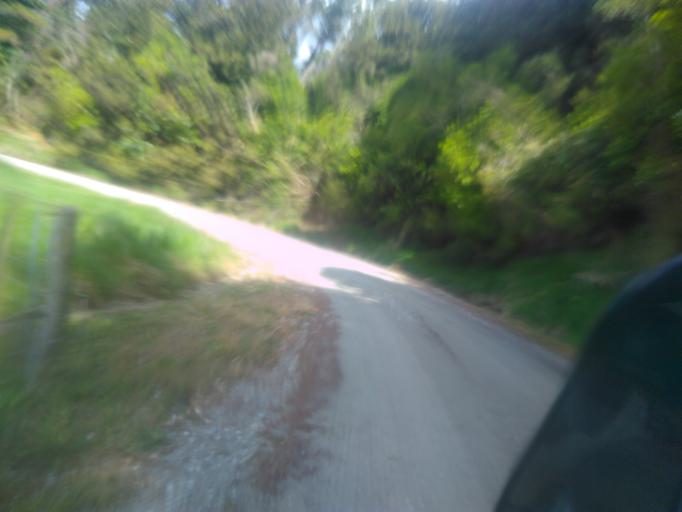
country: NZ
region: Hawke's Bay
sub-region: Wairoa District
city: Wairoa
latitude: -38.7757
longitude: 177.6080
